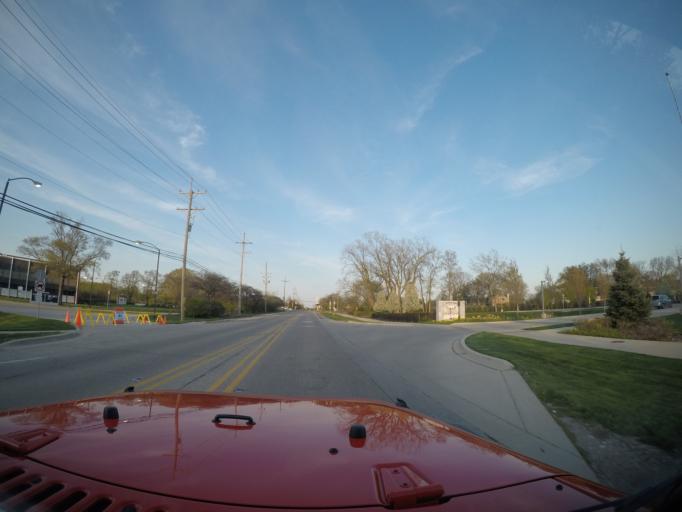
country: US
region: Illinois
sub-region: Cook County
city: Northbrook
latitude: 42.0875
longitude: -87.8462
